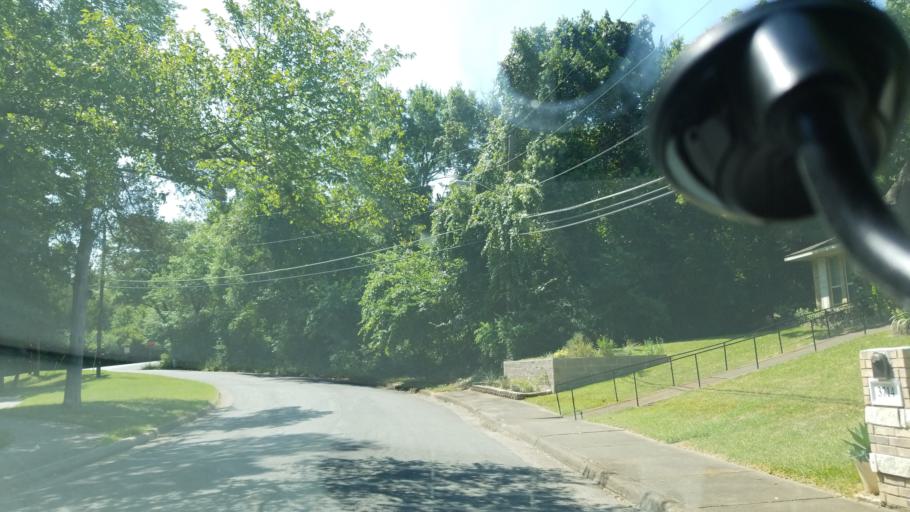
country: US
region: Texas
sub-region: Dallas County
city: Cockrell Hill
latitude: 32.7079
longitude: -96.8817
